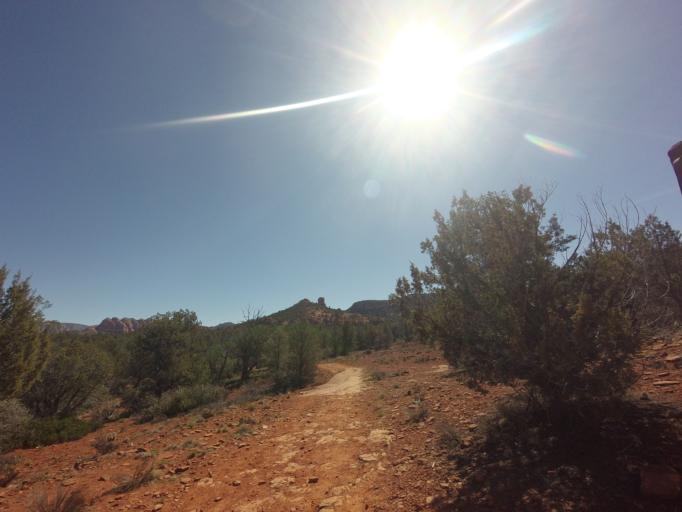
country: US
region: Arizona
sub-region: Yavapai County
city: West Sedona
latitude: 34.8085
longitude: -111.8211
